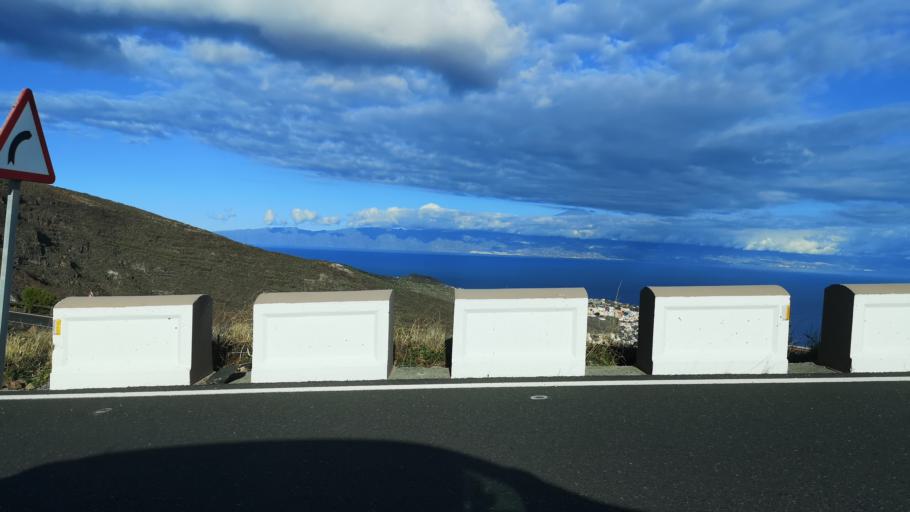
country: ES
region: Canary Islands
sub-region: Provincia de Santa Cruz de Tenerife
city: San Sebastian de la Gomera
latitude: 28.0854
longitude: -17.1376
